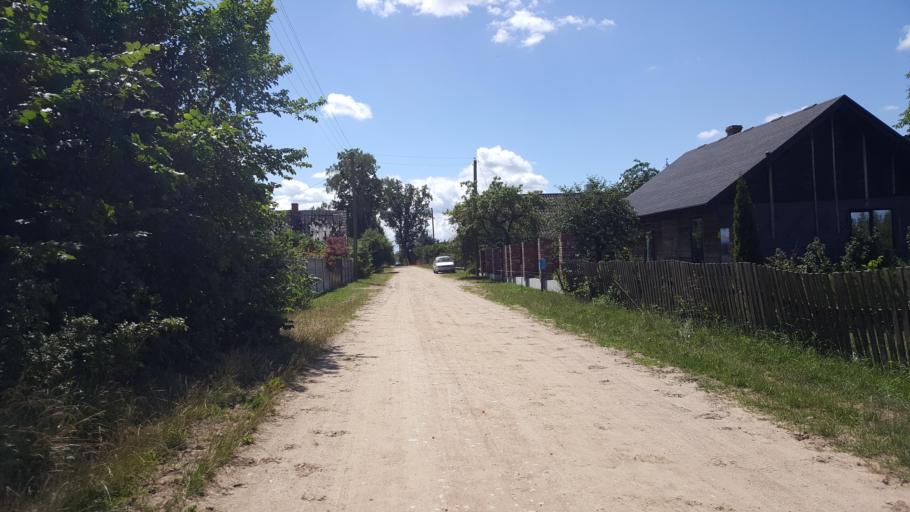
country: BY
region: Brest
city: Kamyanyets
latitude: 52.3286
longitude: 23.9131
